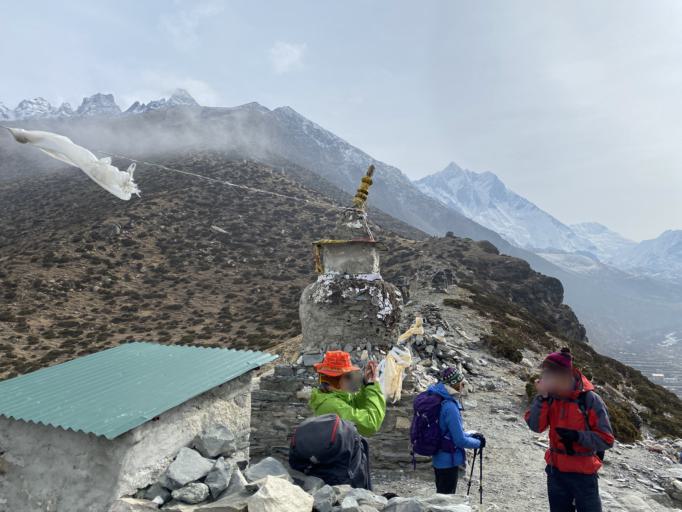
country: NP
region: Eastern Region
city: Lobujya
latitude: 27.8930
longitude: 86.8268
